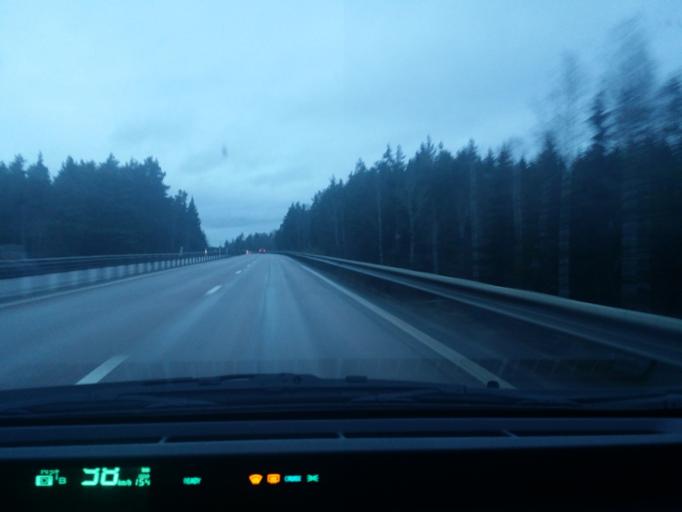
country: SE
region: Soedermanland
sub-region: Eskilstuna Kommun
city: Kvicksund
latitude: 59.4200
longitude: 16.3656
